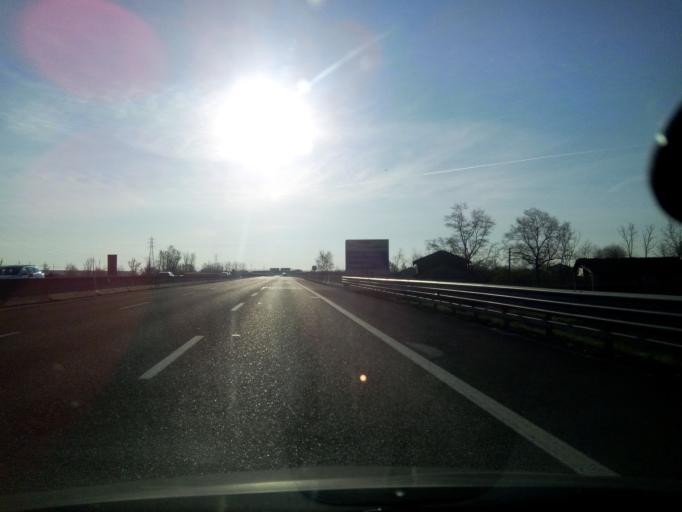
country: IT
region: Emilia-Romagna
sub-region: Provincia di Parma
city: Fidenza
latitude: 44.8903
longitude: 10.0823
